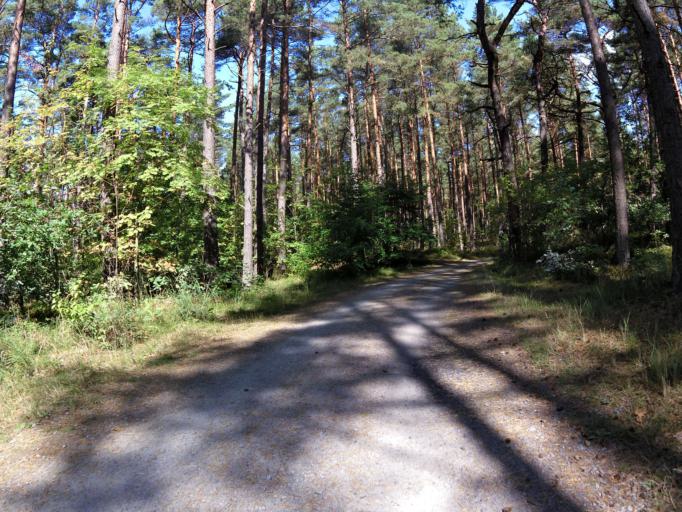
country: DE
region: Mecklenburg-Vorpommern
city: Karlshagen
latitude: 54.1091
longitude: 13.8518
